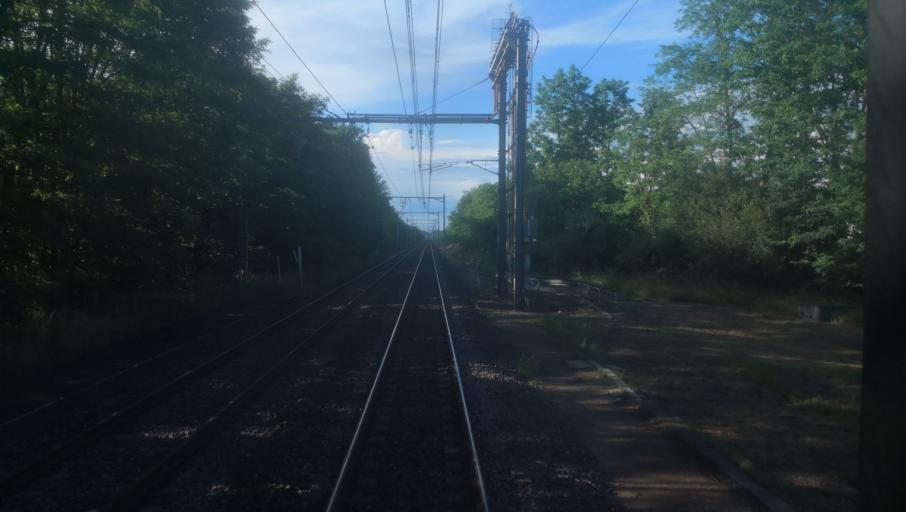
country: FR
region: Centre
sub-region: Departement du Loir-et-Cher
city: Theillay
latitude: 47.3174
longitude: 2.0448
